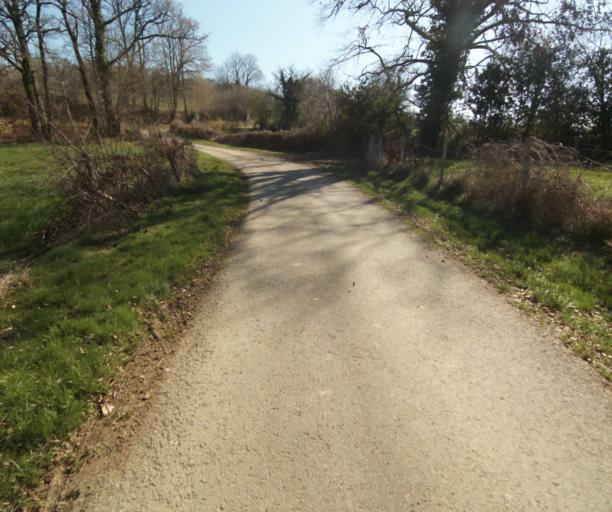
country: FR
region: Limousin
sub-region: Departement de la Correze
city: Saint-Mexant
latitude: 45.2945
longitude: 1.6016
